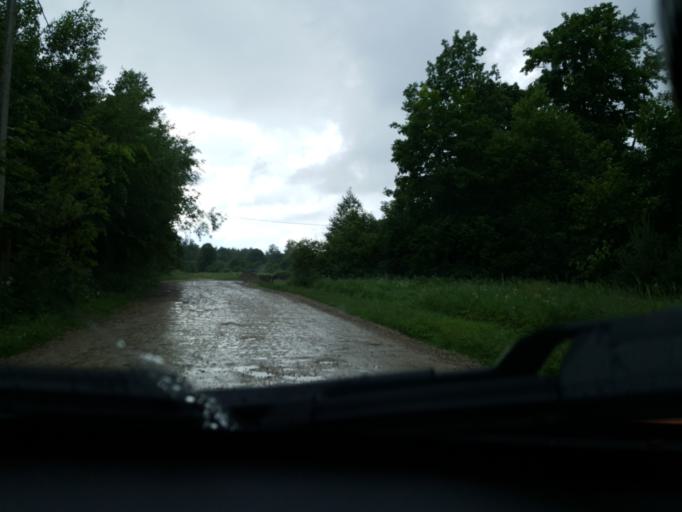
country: LV
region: Ikskile
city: Ikskile
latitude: 56.8933
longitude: 24.5029
